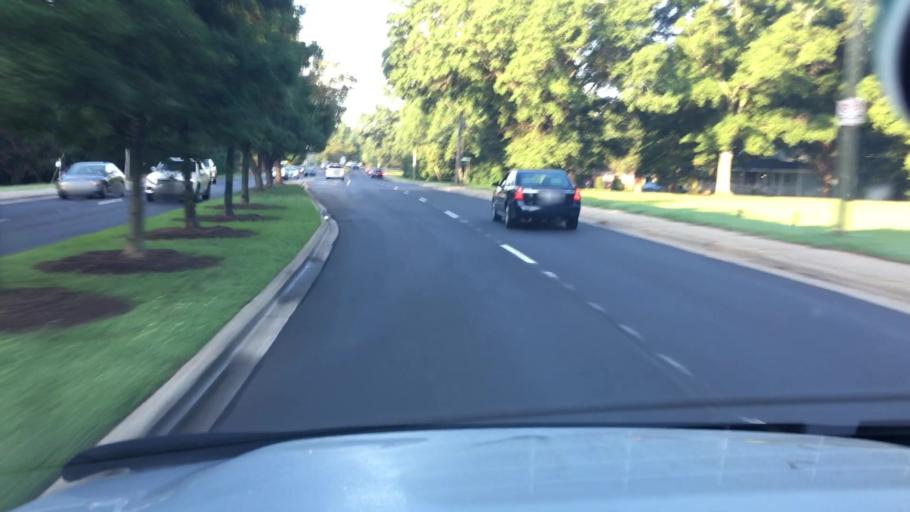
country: US
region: North Carolina
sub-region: Mecklenburg County
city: Pineville
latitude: 35.1033
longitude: -80.8348
